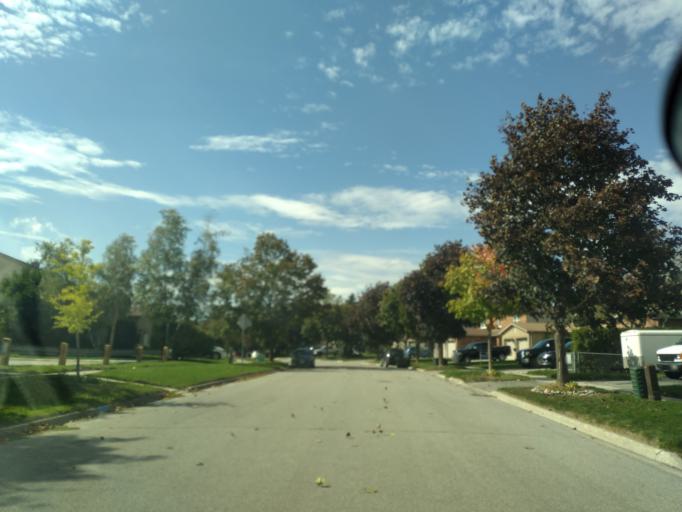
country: CA
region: Ontario
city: Newmarket
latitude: 44.1003
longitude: -79.4845
